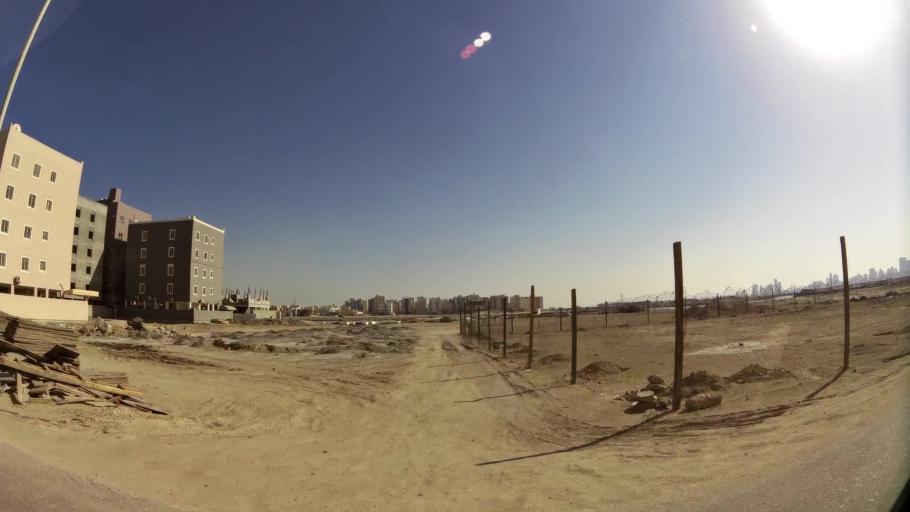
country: BH
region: Muharraq
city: Al Hadd
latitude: 26.2397
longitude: 50.6465
